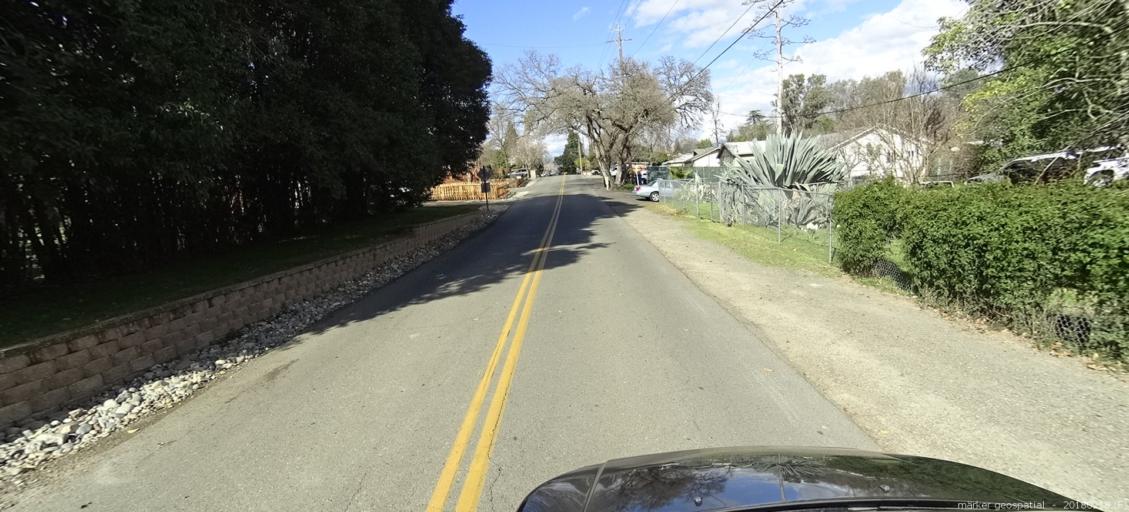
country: US
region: California
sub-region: Sacramento County
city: Orangevale
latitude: 38.6979
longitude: -121.2063
